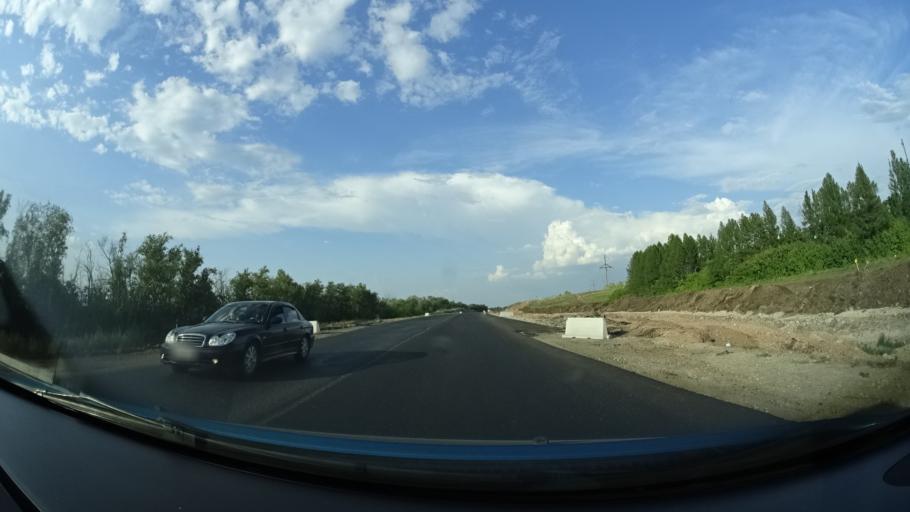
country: RU
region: Samara
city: Sukhodol
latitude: 53.7721
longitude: 50.8966
